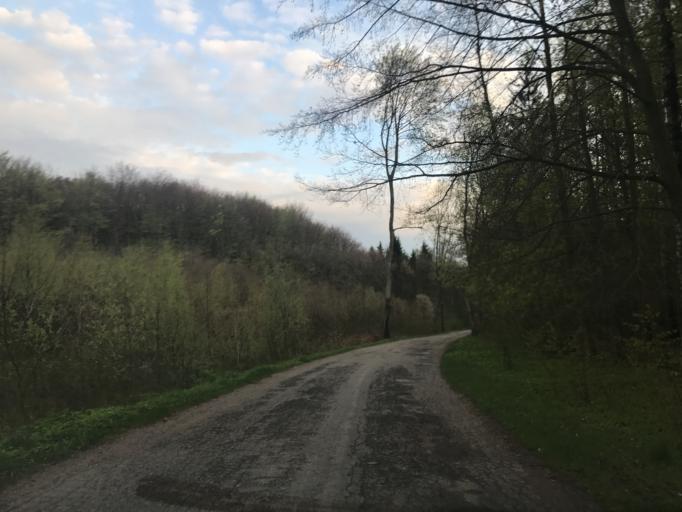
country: PL
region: Warmian-Masurian Voivodeship
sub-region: Powiat ilawski
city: Lubawa
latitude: 53.5527
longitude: 19.8969
